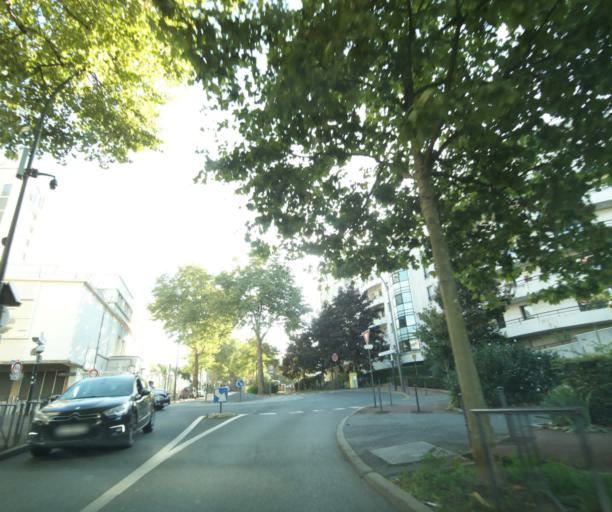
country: FR
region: Ile-de-France
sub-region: Departement des Hauts-de-Seine
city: Fontenay-aux-Roses
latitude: 48.7984
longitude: 2.2832
